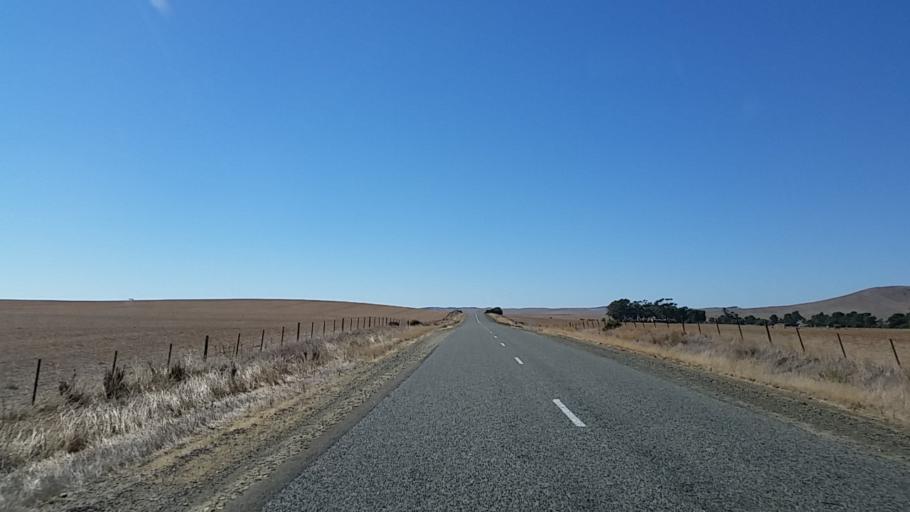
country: AU
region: South Australia
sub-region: Northern Areas
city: Jamestown
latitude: -33.3558
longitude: 138.8875
